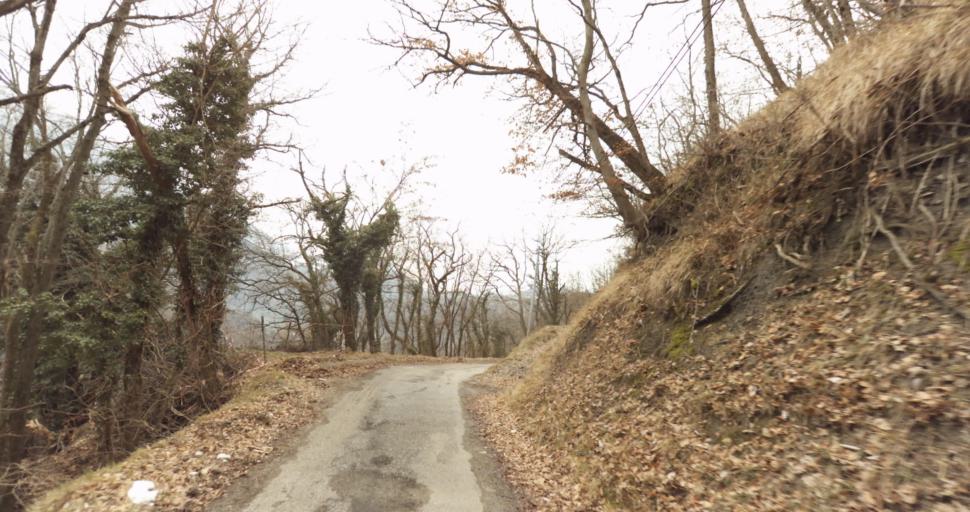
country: FR
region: Rhone-Alpes
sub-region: Departement de l'Isere
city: Saint-Georges-de-Commiers
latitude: 45.0171
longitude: 5.6844
